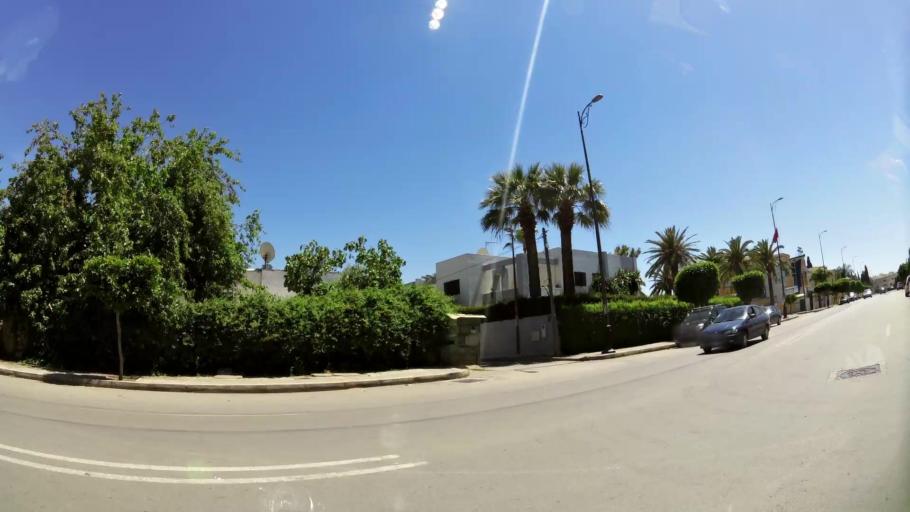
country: MA
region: Fes-Boulemane
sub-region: Fes
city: Fes
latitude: 34.0227
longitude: -4.9994
